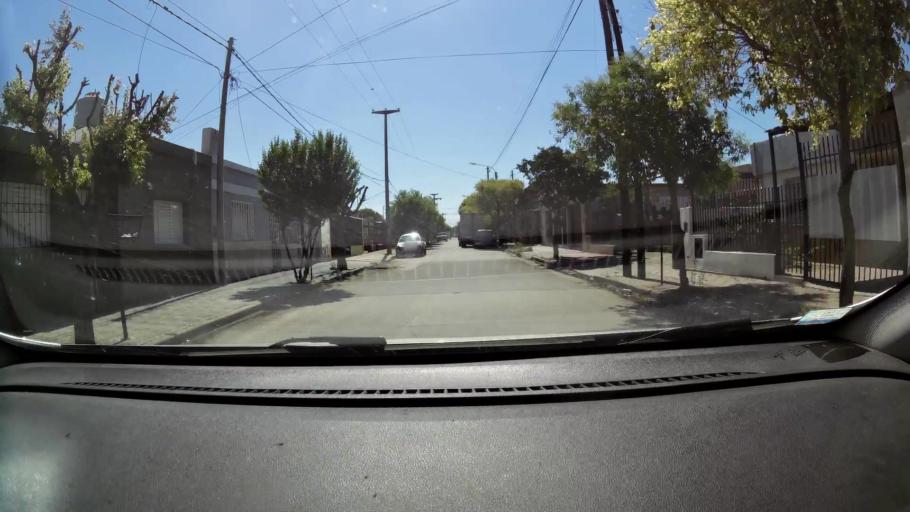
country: AR
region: Cordoba
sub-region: Departamento de Capital
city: Cordoba
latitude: -31.3741
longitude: -64.1531
